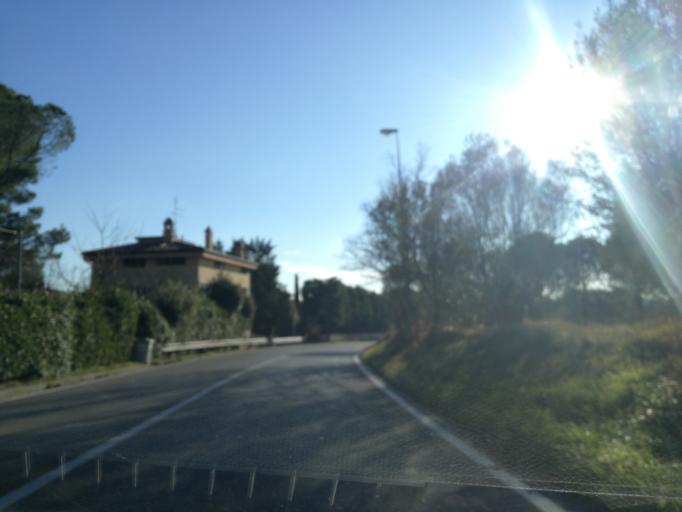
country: IT
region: Umbria
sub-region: Provincia di Perugia
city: Perugia
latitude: 43.0824
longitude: 12.4010
